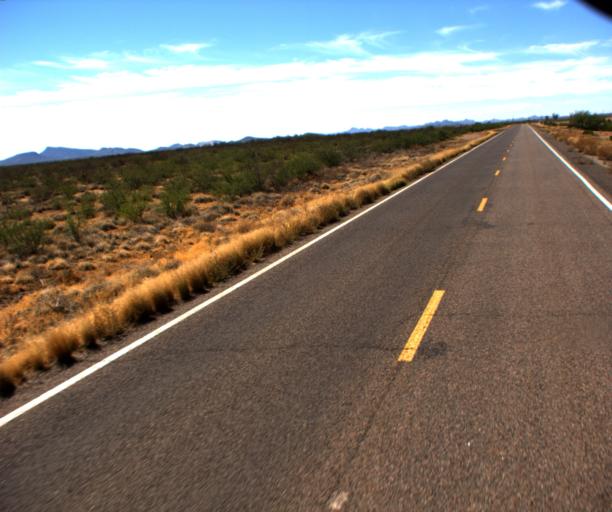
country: US
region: Arizona
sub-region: Yavapai County
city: Congress
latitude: 33.9554
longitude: -113.1416
